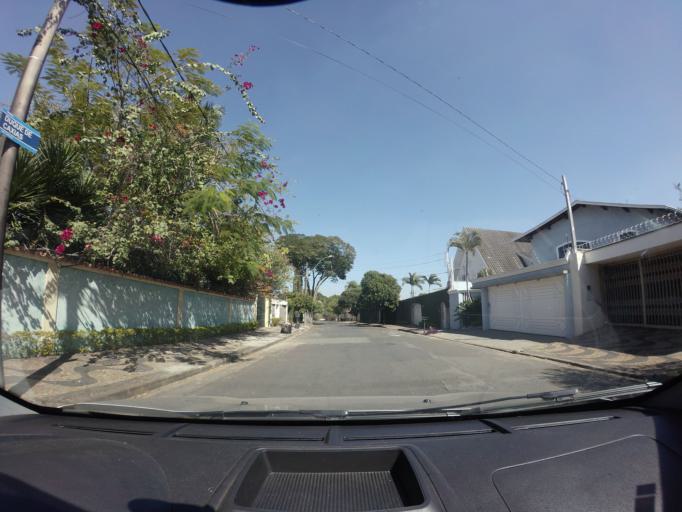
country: BR
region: Sao Paulo
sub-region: Piracicaba
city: Piracicaba
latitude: -22.7153
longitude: -47.6396
